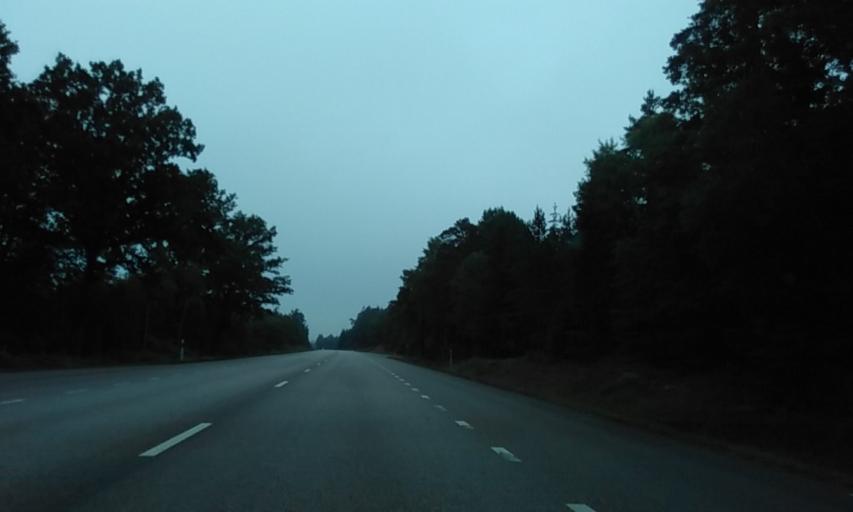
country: SE
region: Vaestra Goetaland
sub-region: Vargarda Kommun
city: Vargarda
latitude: 58.1212
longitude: 12.8497
